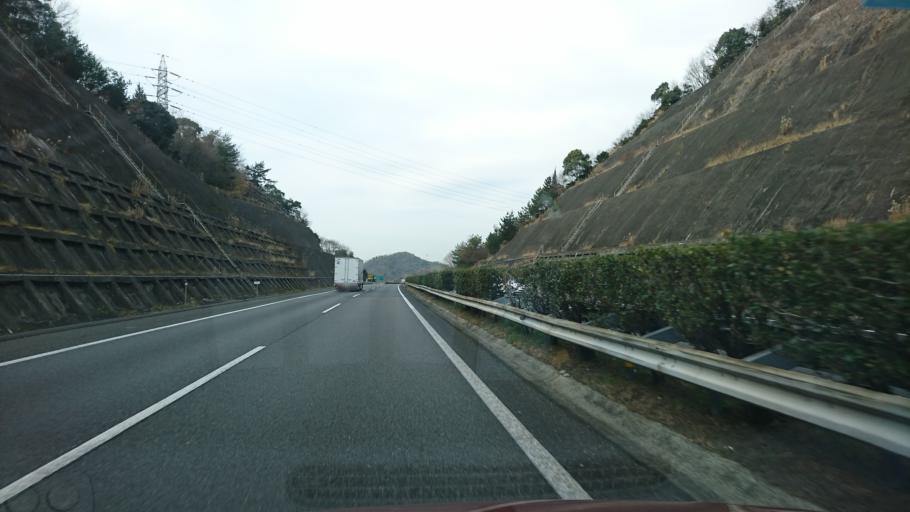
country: JP
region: Okayama
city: Kasaoka
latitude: 34.5319
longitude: 133.5402
